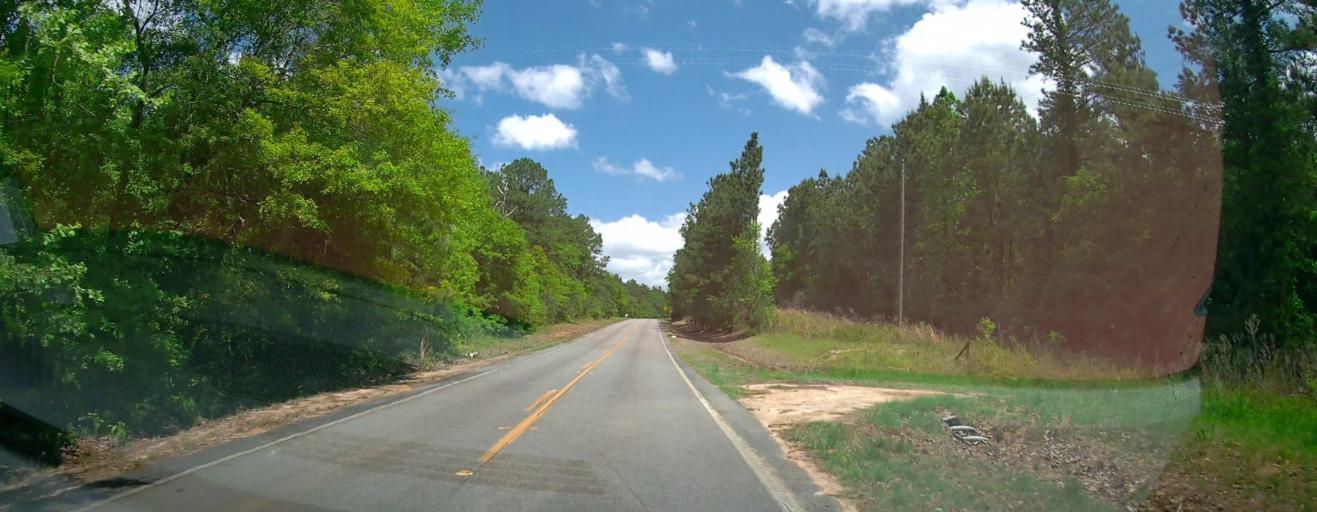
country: US
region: Georgia
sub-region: Bleckley County
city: Cochran
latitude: 32.4550
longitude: -83.2866
